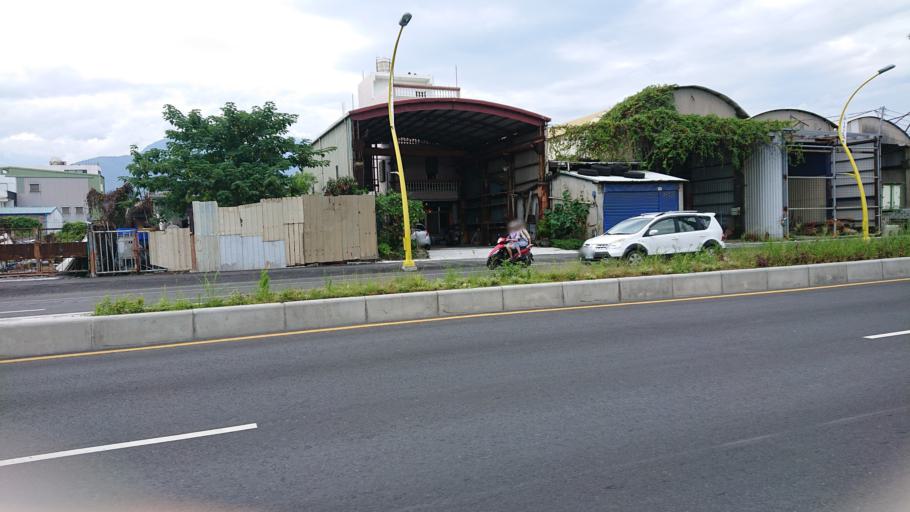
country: TW
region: Taiwan
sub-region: Hualien
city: Hualian
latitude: 23.9499
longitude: 121.5990
